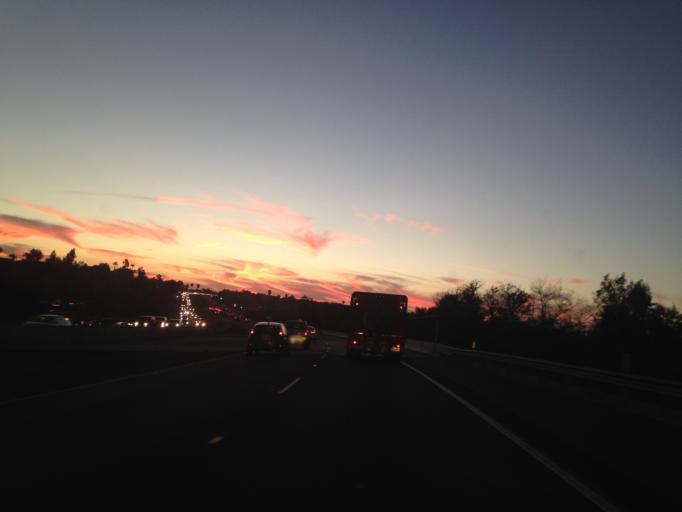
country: US
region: California
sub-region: San Diego County
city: Vista
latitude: 33.2478
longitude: -117.2776
